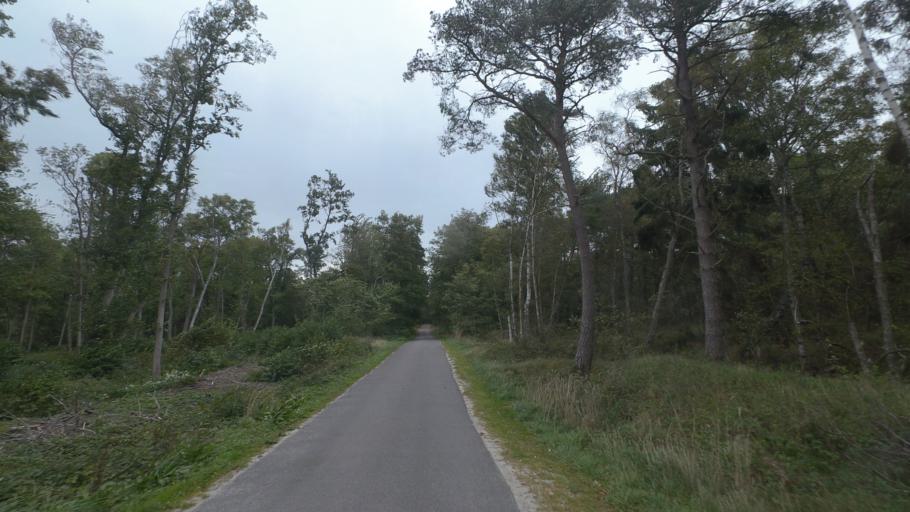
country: DK
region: Capital Region
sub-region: Bornholm Kommune
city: Nexo
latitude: 54.9961
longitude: 15.0381
